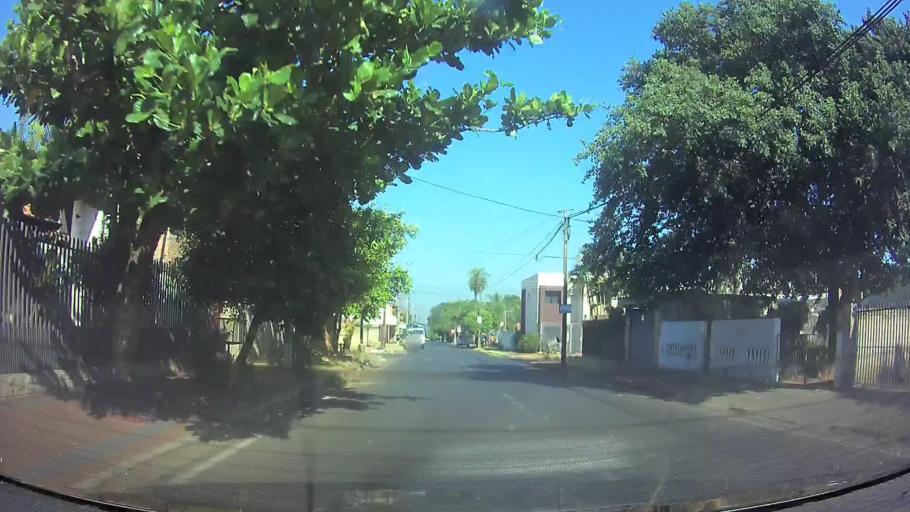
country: PY
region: Central
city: Fernando de la Mora
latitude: -25.2678
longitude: -57.5102
